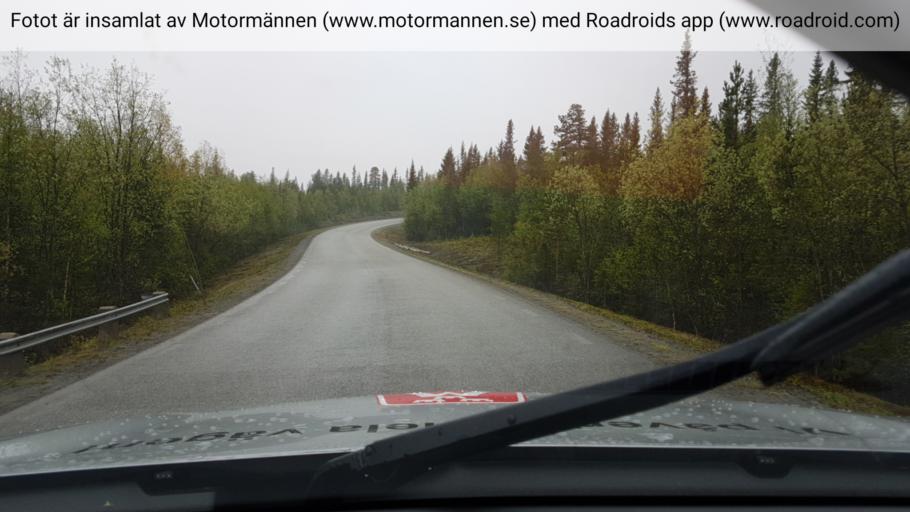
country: SE
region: Jaemtland
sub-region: Krokoms Kommun
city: Valla
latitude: 63.0311
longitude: 13.9500
